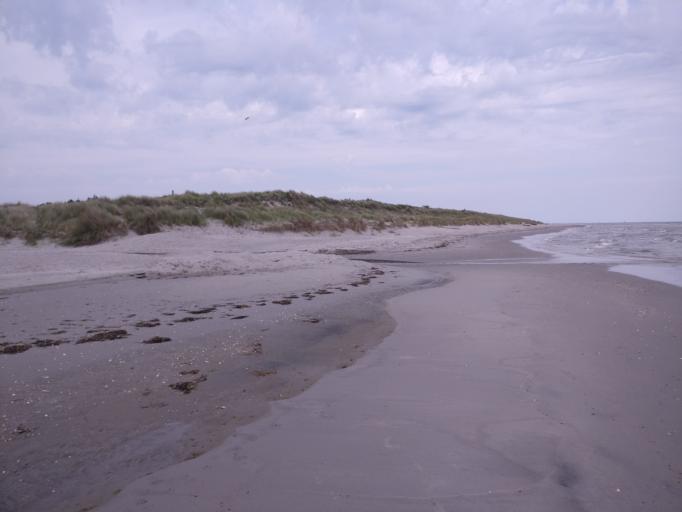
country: DK
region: North Denmark
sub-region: Frederikshavn Kommune
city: Saeby
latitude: 57.2526
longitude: 10.5500
